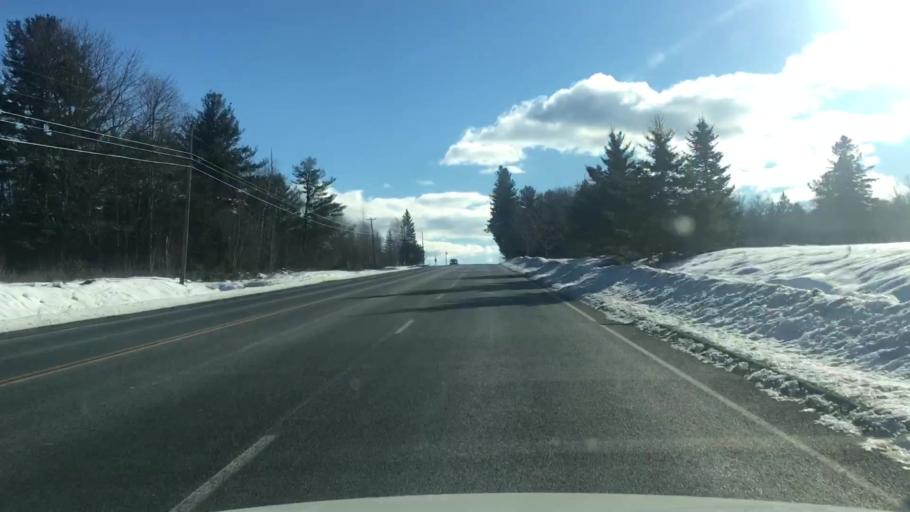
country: US
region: Maine
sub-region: Somerset County
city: Madison
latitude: 44.8955
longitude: -69.8092
